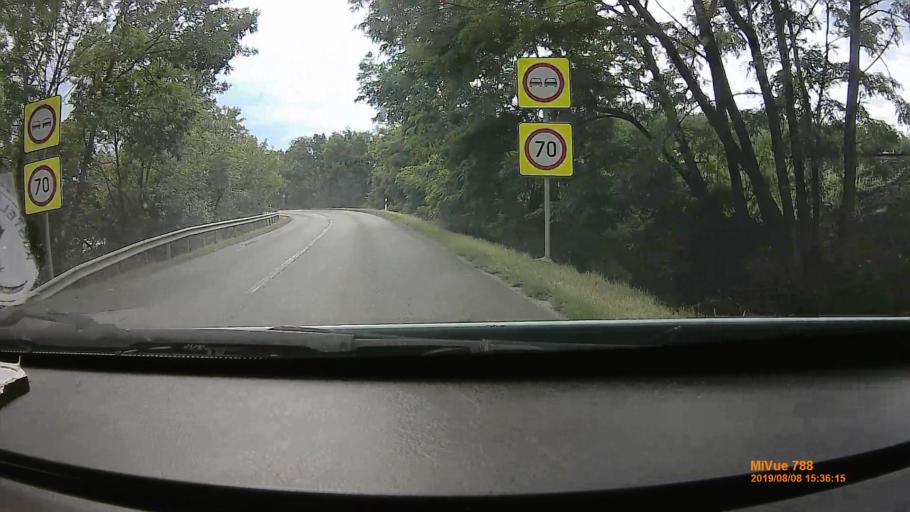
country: HU
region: Szabolcs-Szatmar-Bereg
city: Tunyogmatolcs
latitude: 47.9484
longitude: 22.4299
